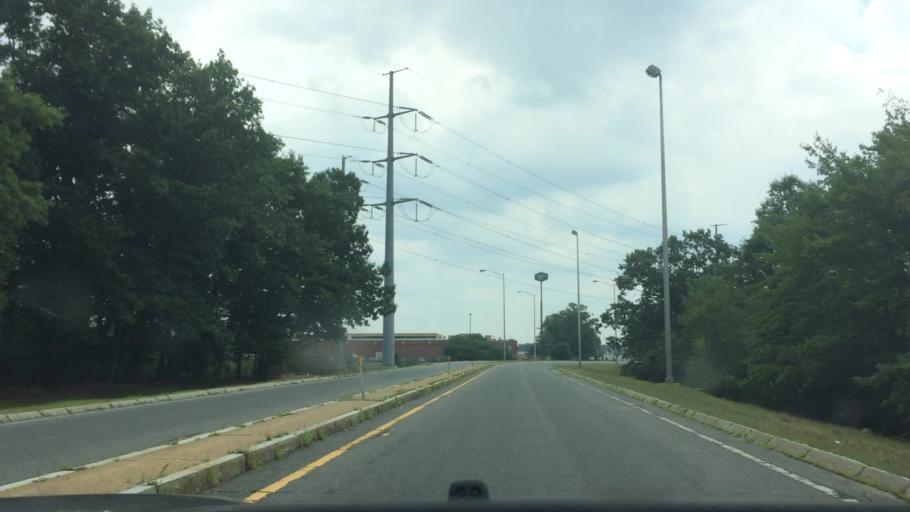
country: US
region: Massachusetts
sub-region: Hampden County
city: North Chicopee
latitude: 42.1732
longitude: -72.5831
